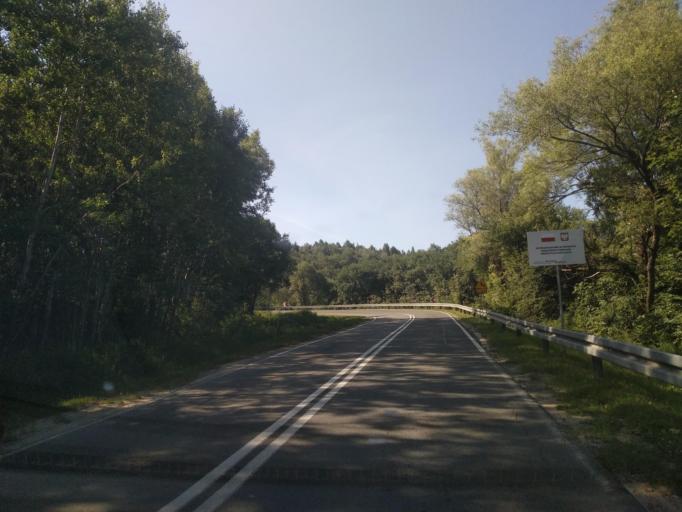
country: PL
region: Subcarpathian Voivodeship
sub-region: Powiat krosnienski
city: Jasliska
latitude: 49.4912
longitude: 21.8080
